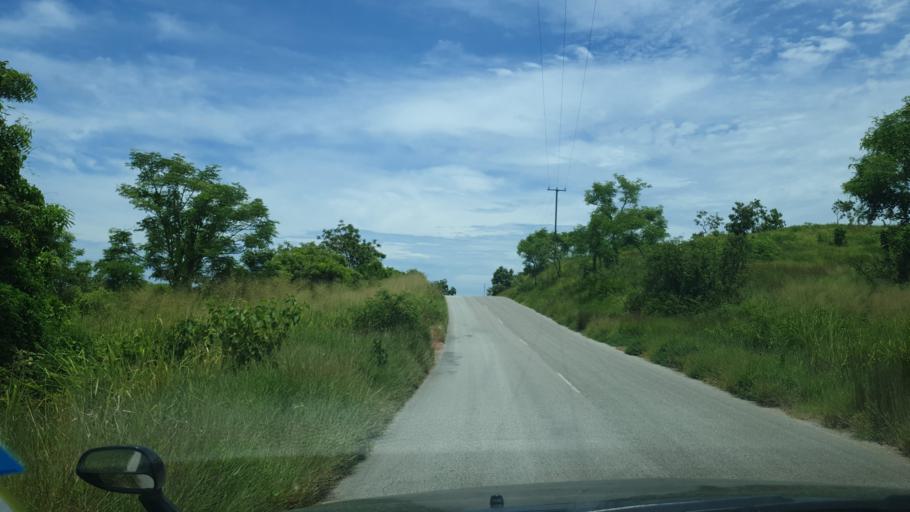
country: PG
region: National Capital
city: Port Moresby
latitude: -9.4286
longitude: 147.0533
